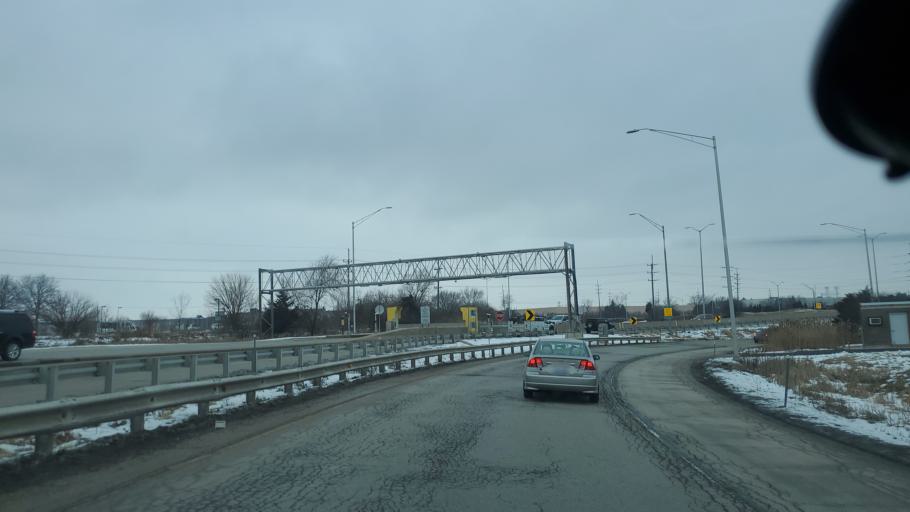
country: US
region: Illinois
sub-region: Kane County
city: North Aurora
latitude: 41.7942
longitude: -88.3265
